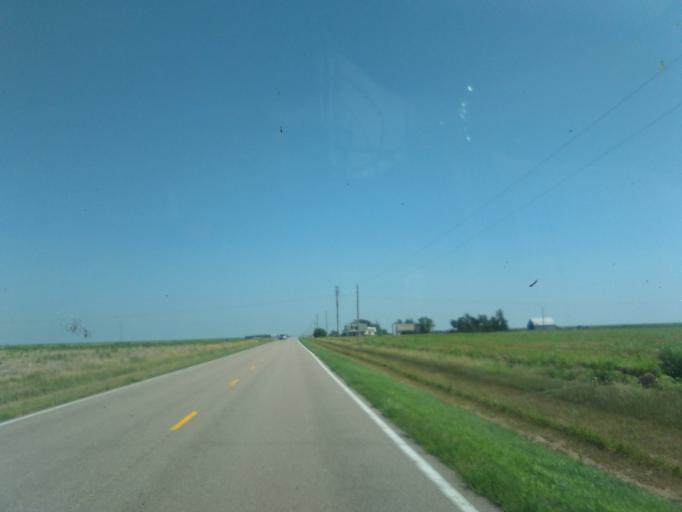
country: US
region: Nebraska
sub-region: Dundy County
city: Benkelman
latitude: 39.8126
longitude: -101.5415
